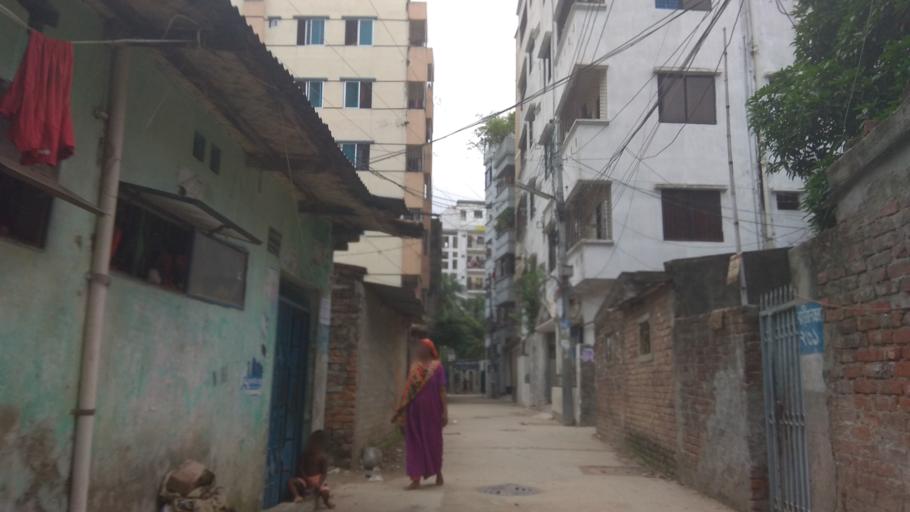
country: BD
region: Dhaka
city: Azimpur
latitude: 23.8010
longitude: 90.3755
